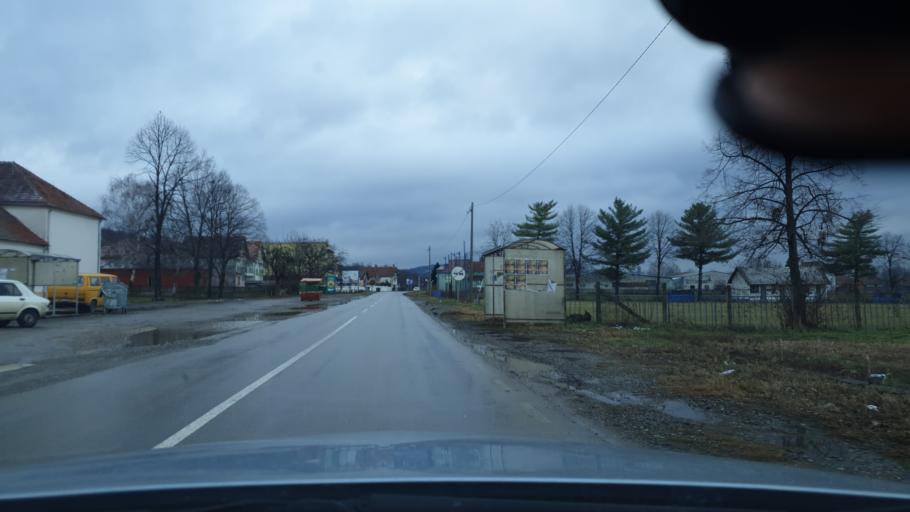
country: RS
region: Central Serbia
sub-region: Branicevski Okrug
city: Petrovac
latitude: 44.4044
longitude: 21.3969
